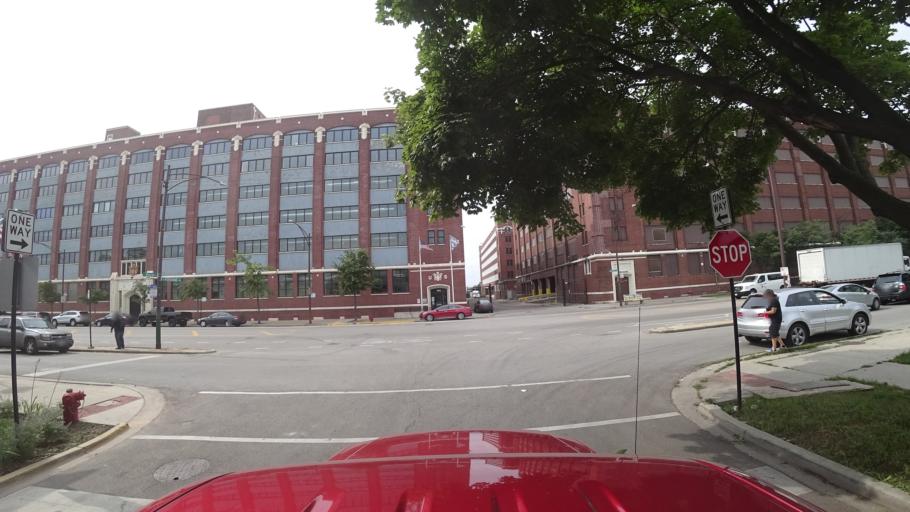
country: US
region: Illinois
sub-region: Cook County
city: Chicago
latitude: 41.8234
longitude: -87.6727
